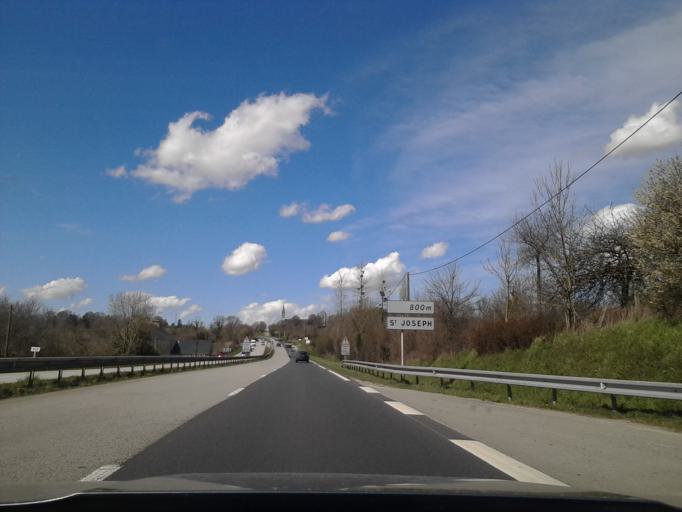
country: FR
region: Lower Normandy
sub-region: Departement de la Manche
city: Valognes
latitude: 49.5269
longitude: -1.5129
